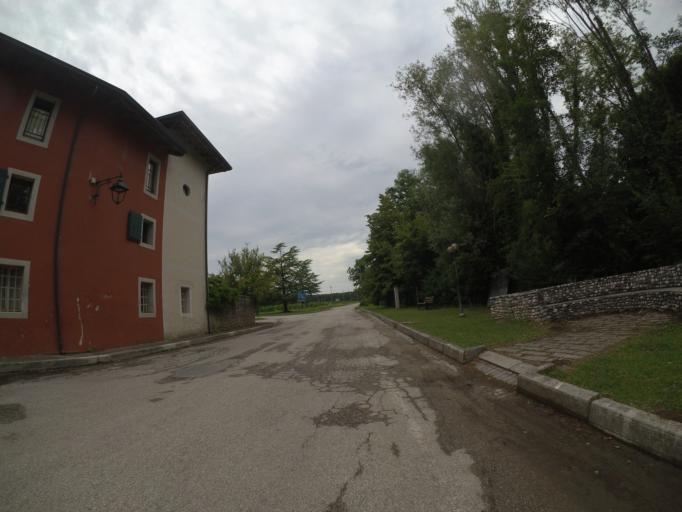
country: IT
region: Friuli Venezia Giulia
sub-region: Provincia di Udine
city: Rivignano
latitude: 45.9048
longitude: 13.0505
